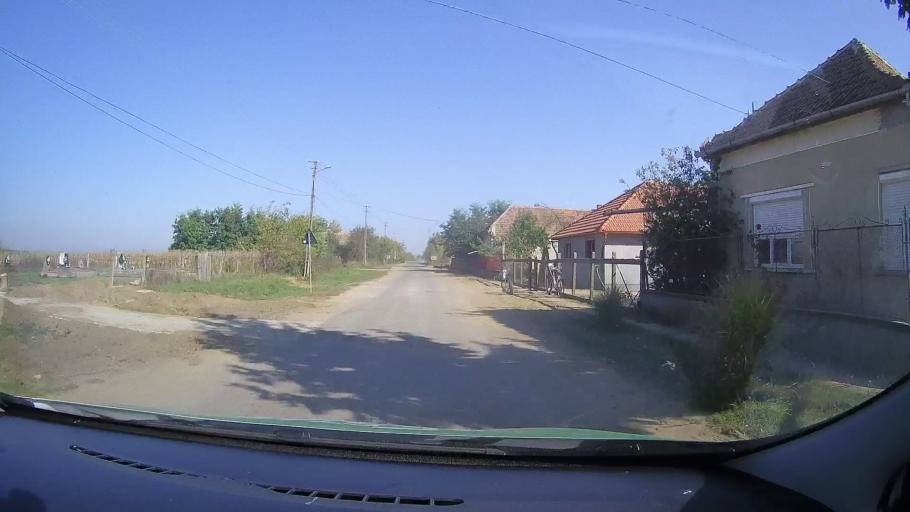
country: RO
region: Satu Mare
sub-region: Comuna Ciumesti
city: Ciumesti
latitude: 47.6712
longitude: 22.3415
